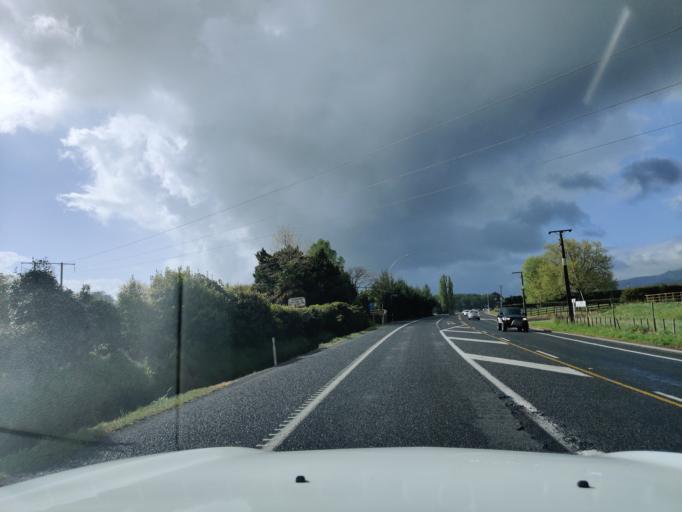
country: NZ
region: Waikato
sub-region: Waipa District
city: Cambridge
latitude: -37.9278
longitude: 175.5698
